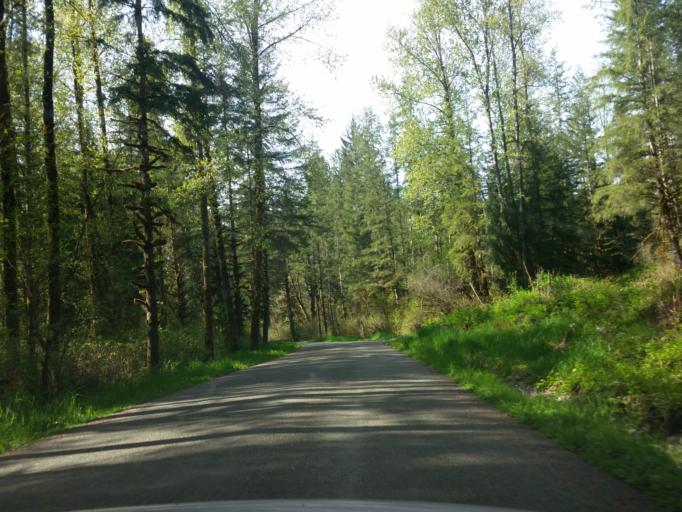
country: US
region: Washington
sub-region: Snohomish County
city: Woods Creek
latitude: 47.9760
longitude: -121.8764
